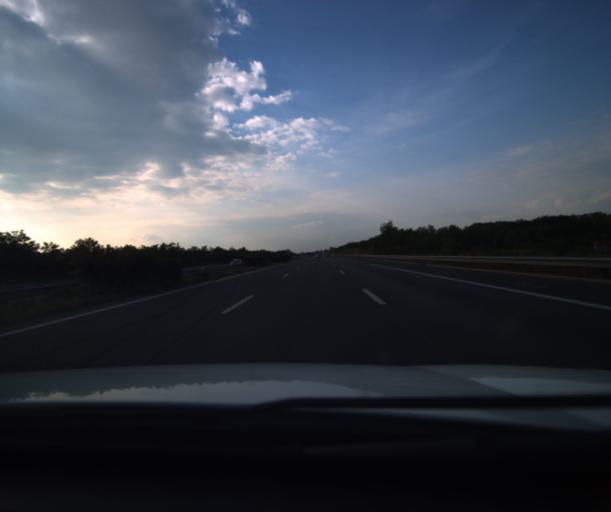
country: FR
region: Midi-Pyrenees
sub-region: Departement du Tarn-et-Garonne
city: Pompignan
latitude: 43.8247
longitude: 1.3457
